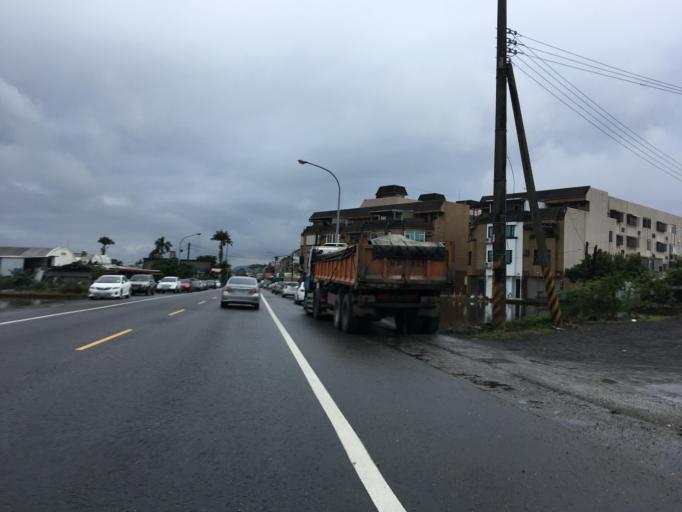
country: TW
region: Taiwan
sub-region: Yilan
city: Yilan
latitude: 24.6579
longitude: 121.7581
